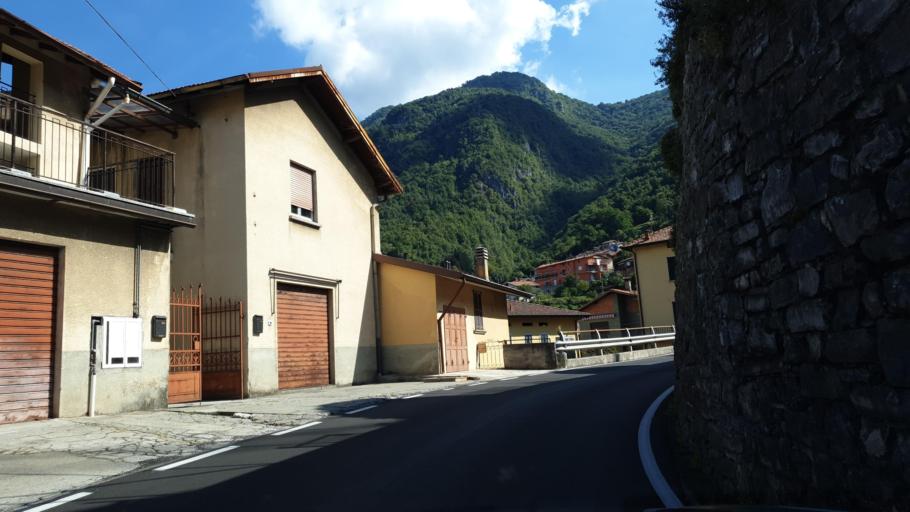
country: IT
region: Lombardy
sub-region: Provincia di Como
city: Lezzeno
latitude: 45.9487
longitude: 9.2045
